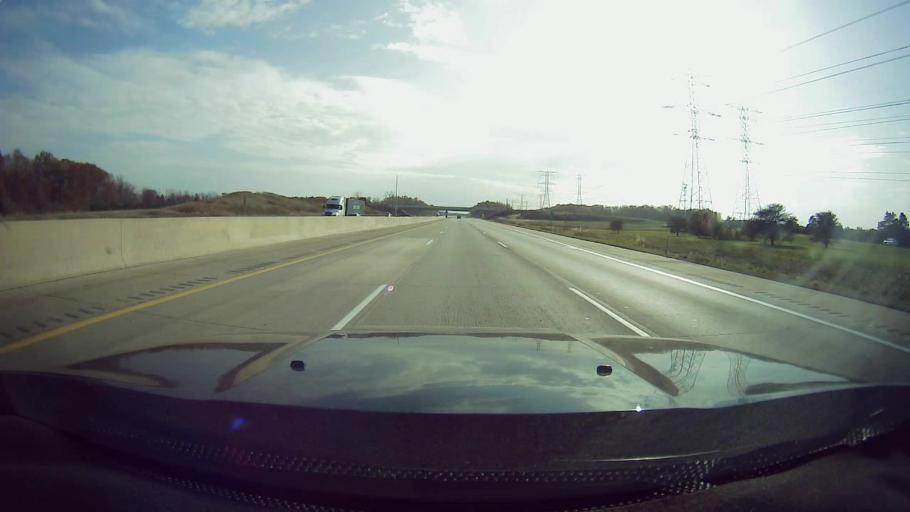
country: US
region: Michigan
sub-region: Wayne County
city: Woodhaven
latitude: 42.1055
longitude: -83.2416
